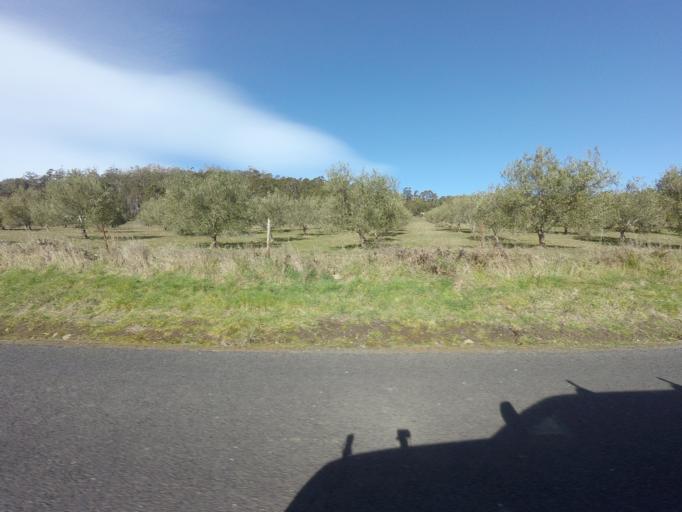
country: AU
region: Tasmania
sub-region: Huon Valley
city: Cygnet
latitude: -43.1791
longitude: 147.1422
